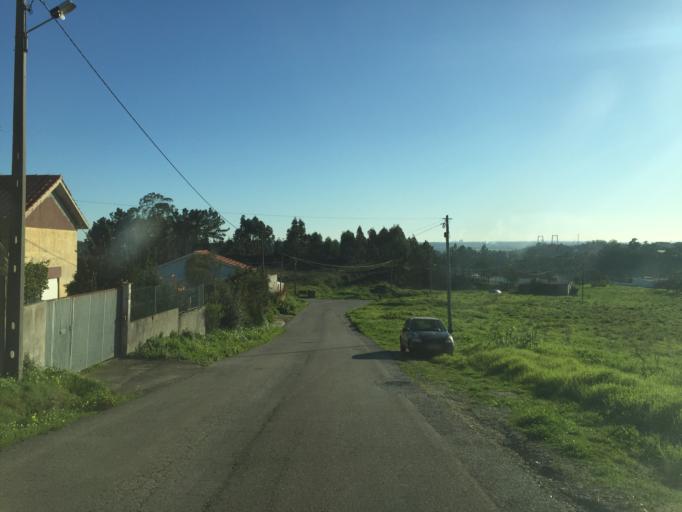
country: PT
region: Coimbra
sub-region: Figueira da Foz
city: Tavarede
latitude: 40.1685
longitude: -8.8332
